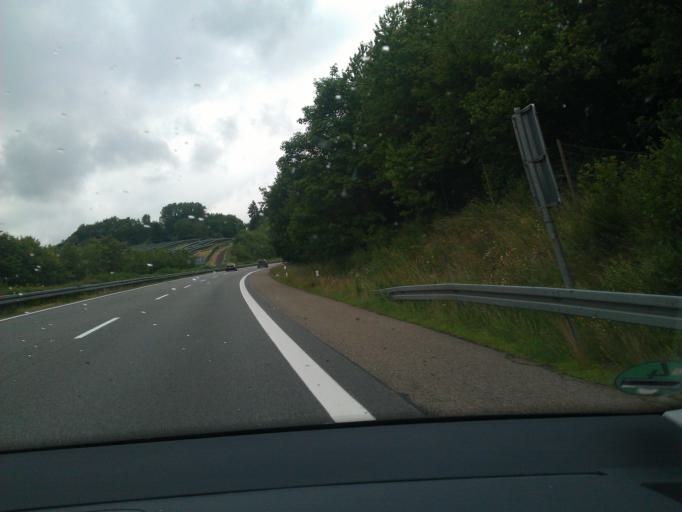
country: DE
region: Rheinland-Pfalz
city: Achtelsbach
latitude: 49.5892
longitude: 7.0620
